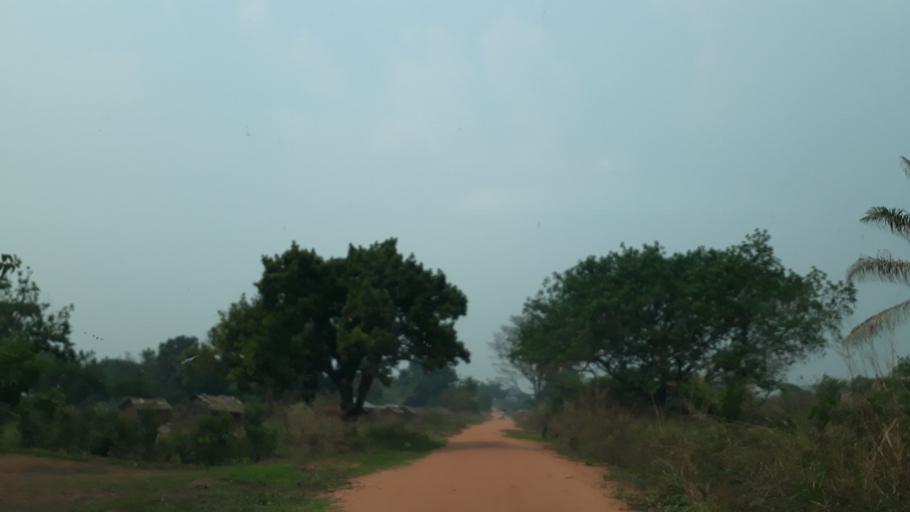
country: CD
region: Kasai-Occidental
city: Tshikapa
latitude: -6.4843
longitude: 20.4271
